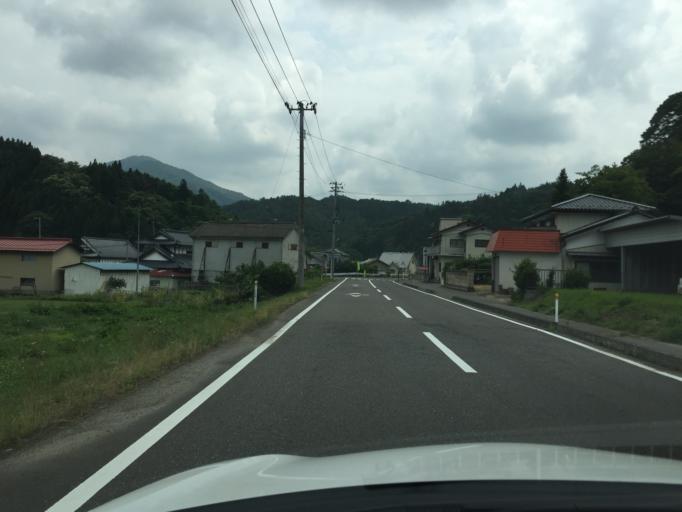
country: JP
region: Fukushima
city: Miharu
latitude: 37.2942
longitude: 140.5389
